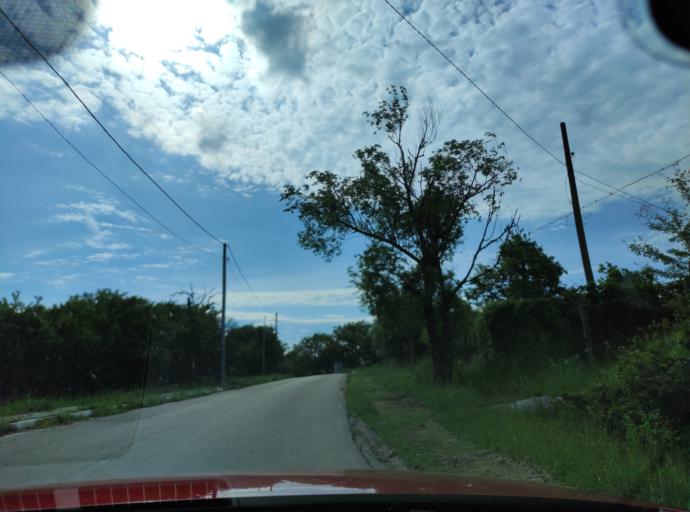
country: BG
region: Vidin
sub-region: Obshtina Belogradchik
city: Belogradchik
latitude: 43.5141
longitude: 22.7384
